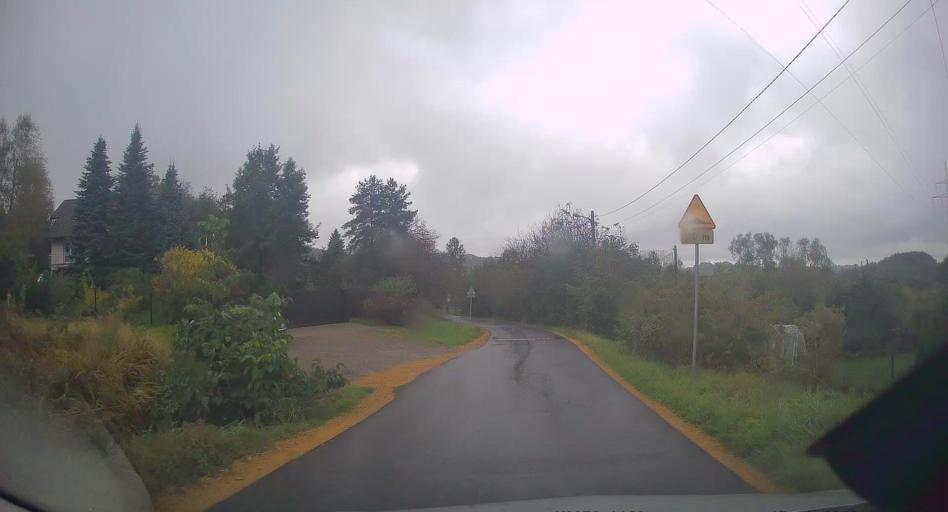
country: PL
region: Lesser Poland Voivodeship
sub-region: Powiat krakowski
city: Ochojno
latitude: 49.9839
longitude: 19.9893
